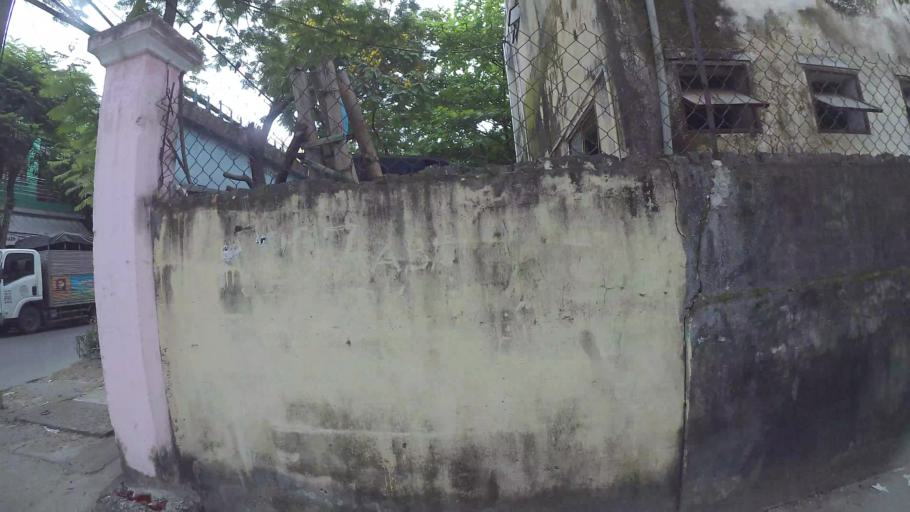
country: VN
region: Da Nang
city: Lien Chieu
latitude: 16.0767
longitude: 108.1718
